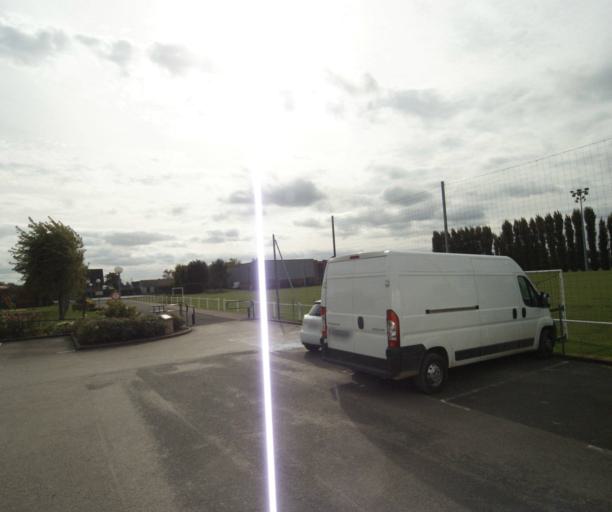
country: FR
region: Nord-Pas-de-Calais
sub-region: Departement du Nord
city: Bois-Grenier
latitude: 50.6455
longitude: 2.8765
